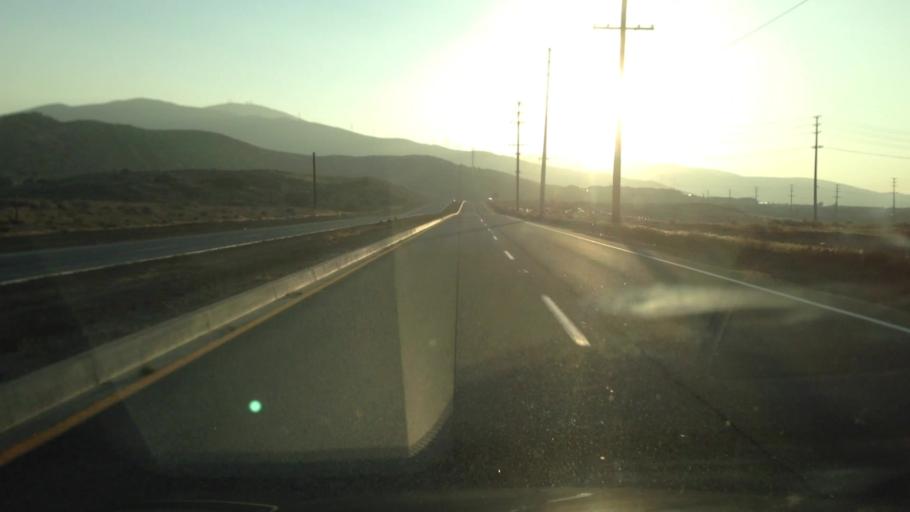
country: US
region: California
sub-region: Los Angeles County
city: Desert View Highlands
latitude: 34.5582
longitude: -118.1564
